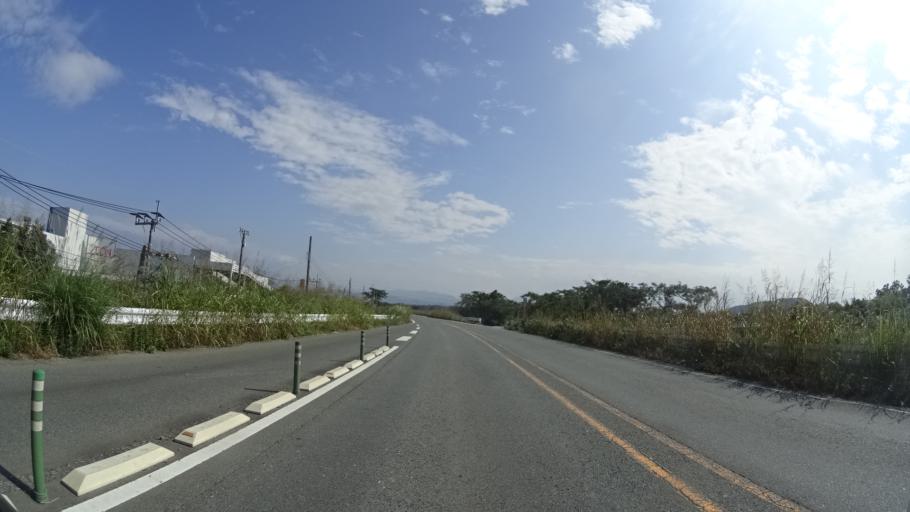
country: JP
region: Kumamoto
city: Kumamoto
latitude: 32.7369
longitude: 130.7432
